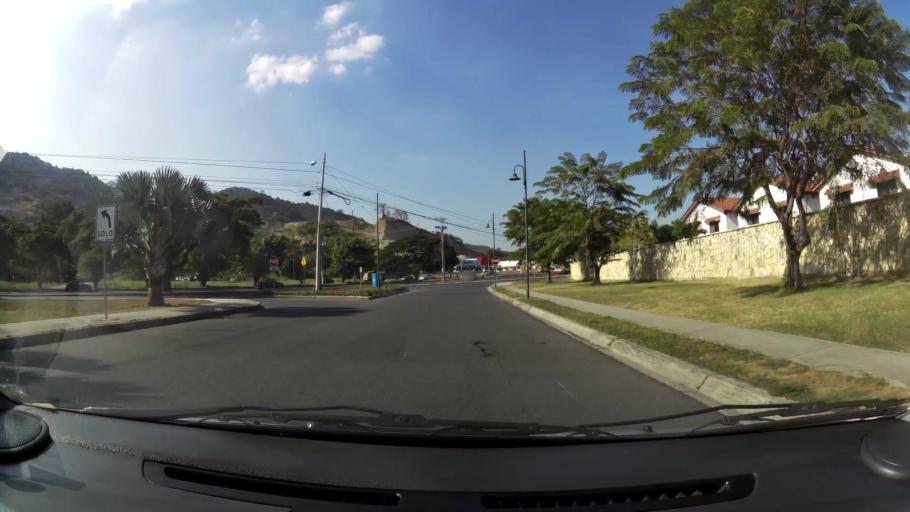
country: EC
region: Guayas
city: Santa Lucia
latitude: -2.1838
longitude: -79.9974
